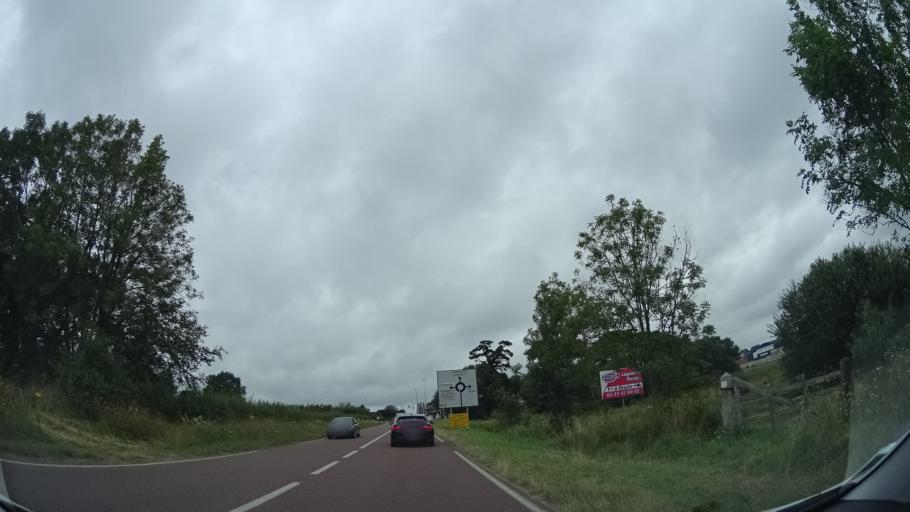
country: FR
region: Lower Normandy
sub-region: Departement de la Manche
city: La Haye-du-Puits
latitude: 49.2765
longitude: -1.5405
